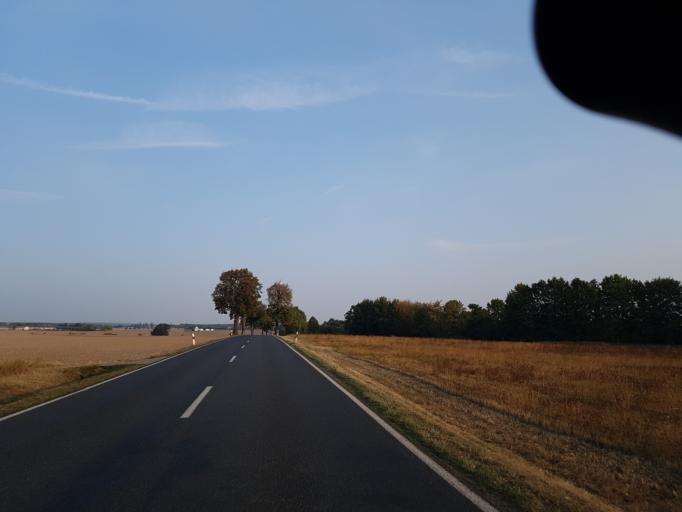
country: DE
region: Saxony
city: Elsnig
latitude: 51.5978
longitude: 12.9445
